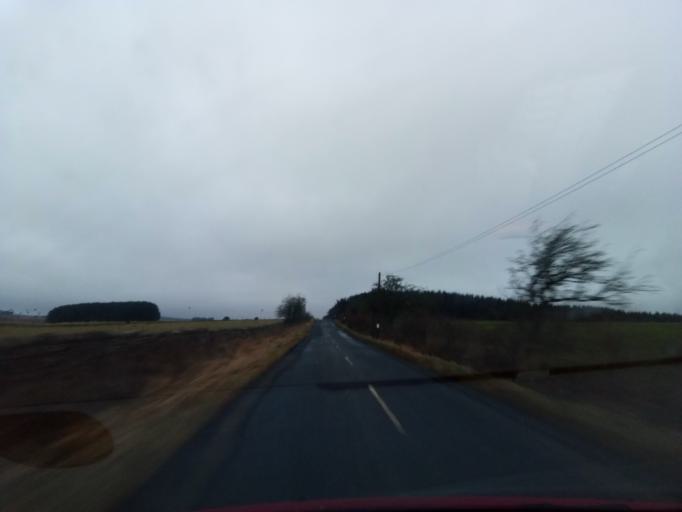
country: GB
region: England
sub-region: Northumberland
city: Rothley
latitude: 55.2002
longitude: -1.9829
